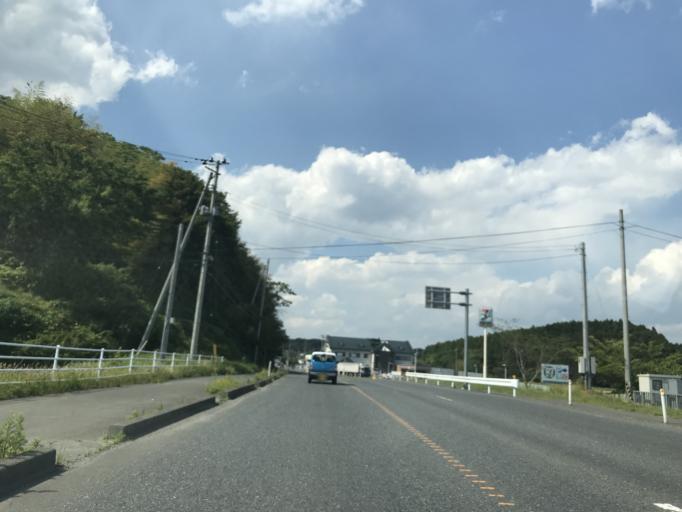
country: JP
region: Miyagi
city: Wakuya
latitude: 38.4817
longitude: 141.1084
